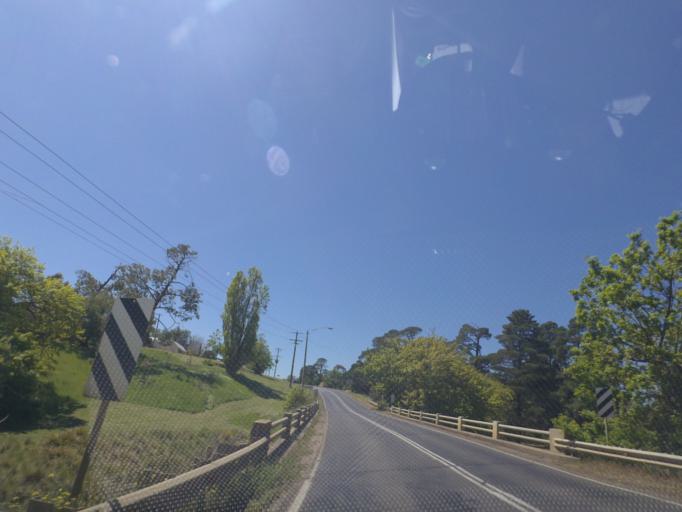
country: AU
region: Victoria
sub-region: Hume
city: Sunbury
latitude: -37.4652
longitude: 144.6733
